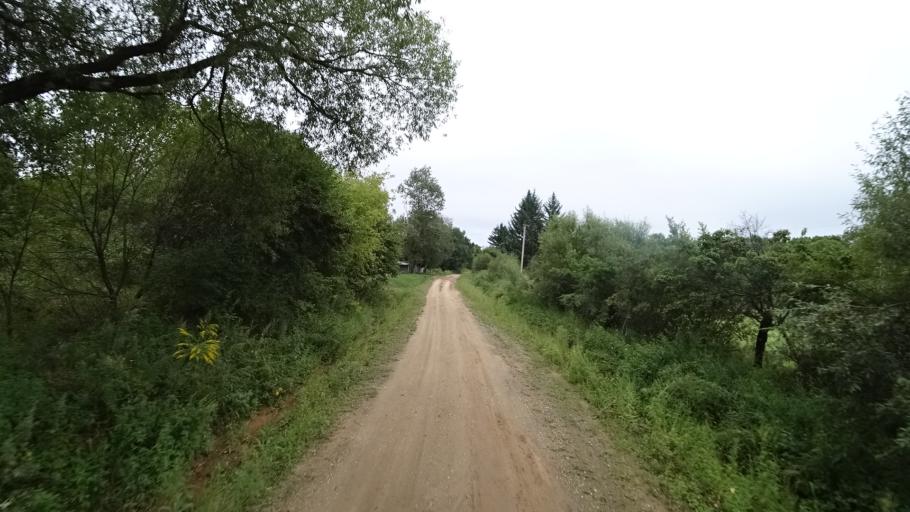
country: RU
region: Primorskiy
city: Rettikhovka
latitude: 44.1629
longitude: 132.7423
